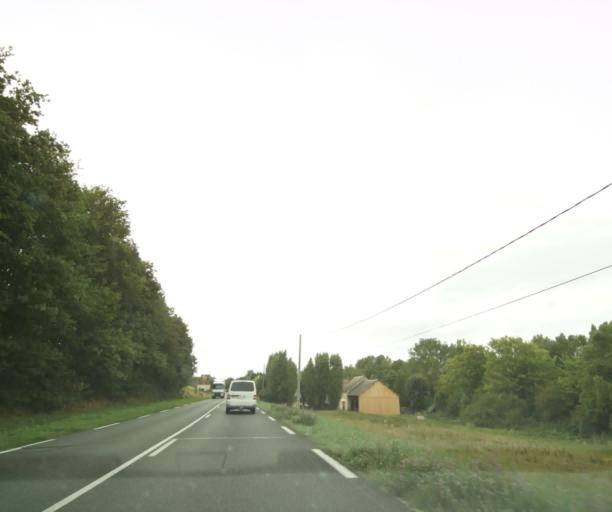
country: FR
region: Centre
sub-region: Departement d'Indre-et-Loire
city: Perrusson
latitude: 47.0702
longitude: 1.0763
